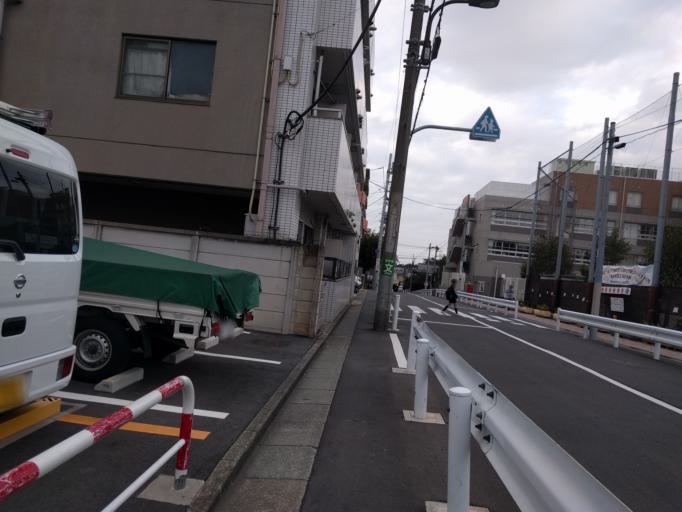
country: JP
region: Tokyo
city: Tokyo
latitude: 35.6423
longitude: 139.6447
